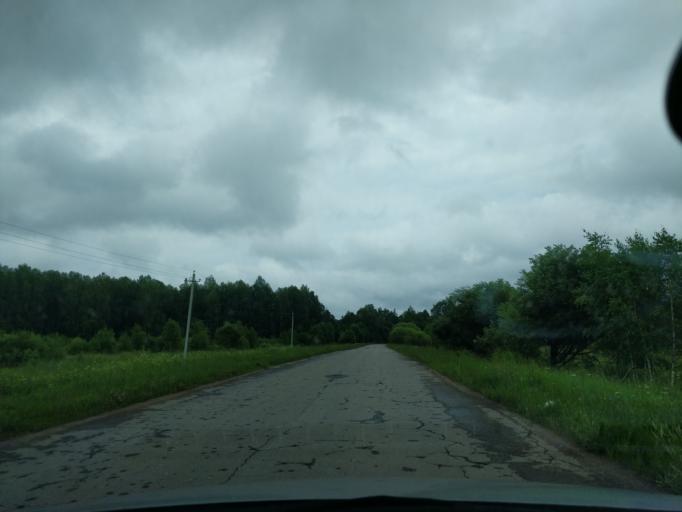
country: RU
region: Kaluga
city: Myatlevo
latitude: 54.8401
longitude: 35.6300
